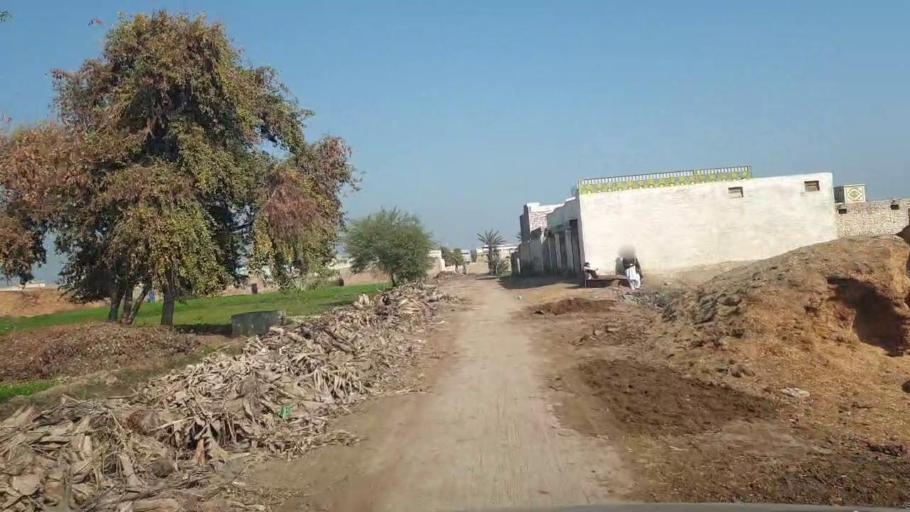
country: PK
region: Sindh
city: Shahdadpur
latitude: 25.9444
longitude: 68.5924
